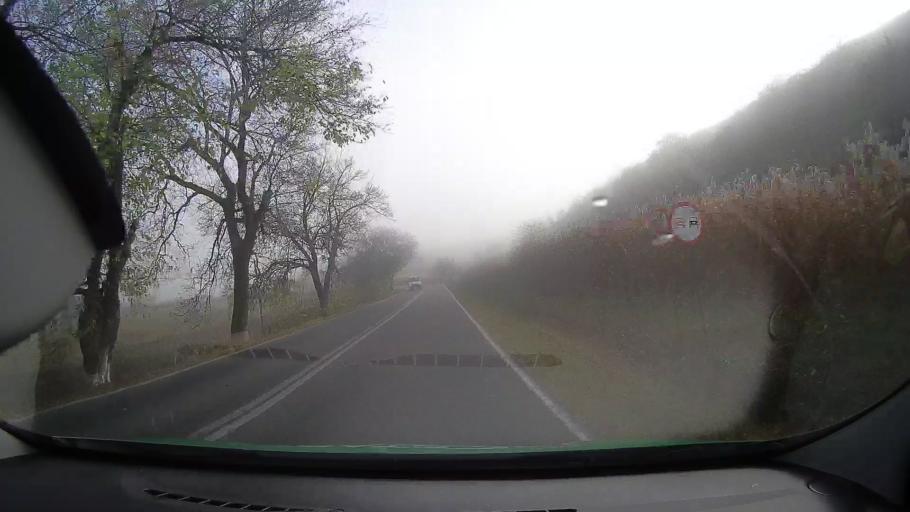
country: RO
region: Tulcea
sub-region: Comuna Nufaru
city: Malcoci
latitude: 45.1460
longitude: 28.9005
